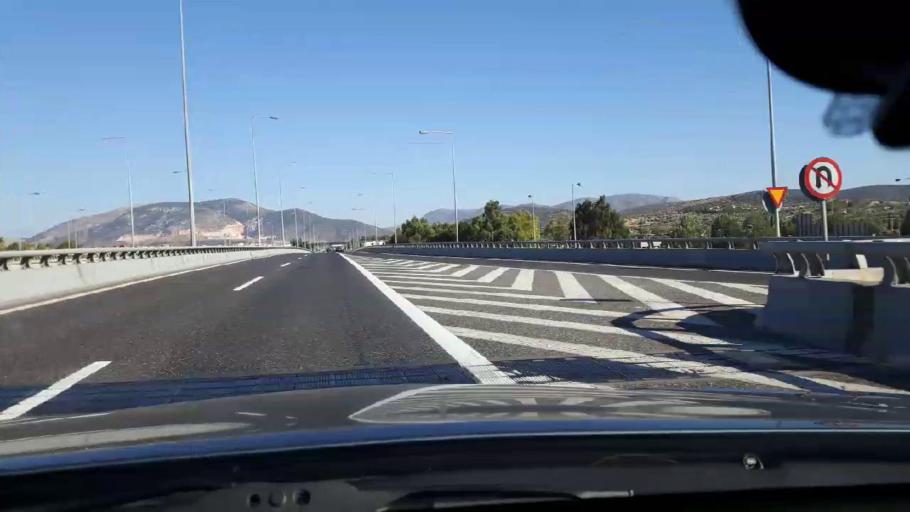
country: GR
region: Attica
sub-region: Nomarchia Anatolikis Attikis
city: Markopoulo
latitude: 37.8981
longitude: 23.9079
